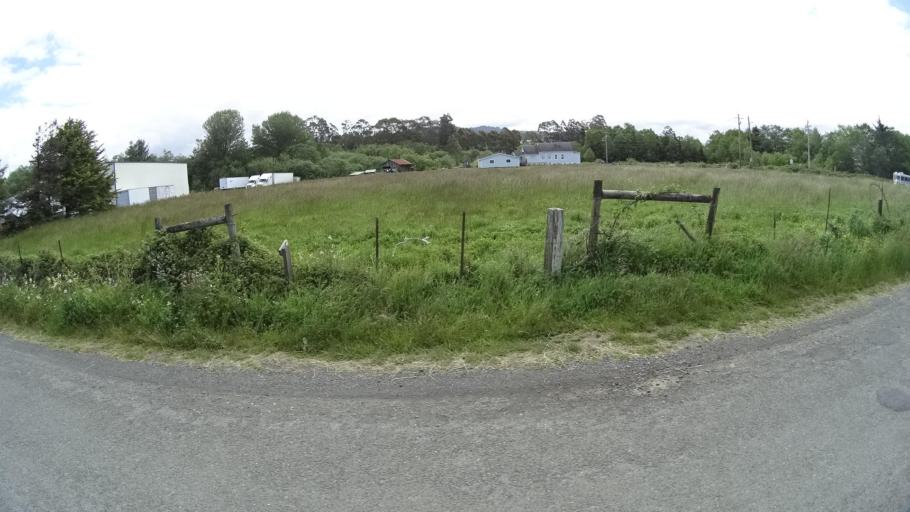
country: US
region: California
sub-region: Humboldt County
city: Arcata
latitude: 40.8779
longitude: -124.0949
